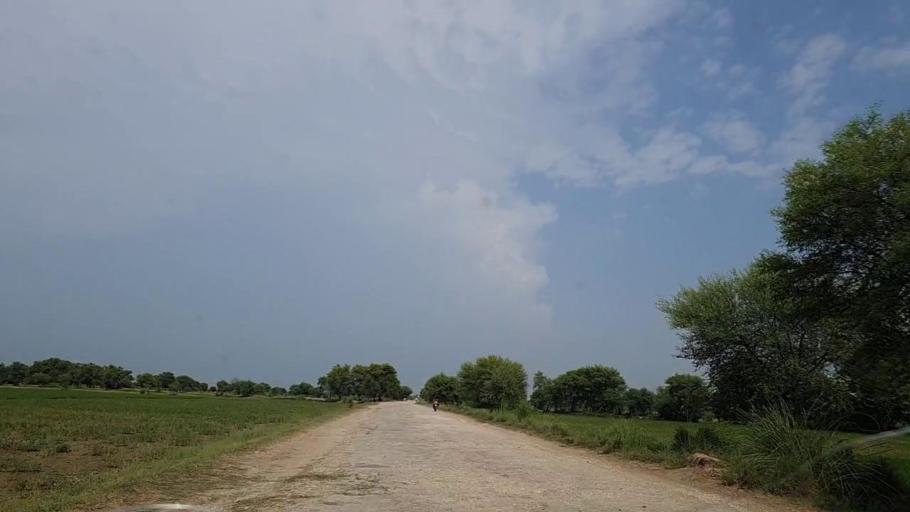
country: PK
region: Sindh
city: Khanpur
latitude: 27.8480
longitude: 69.4306
